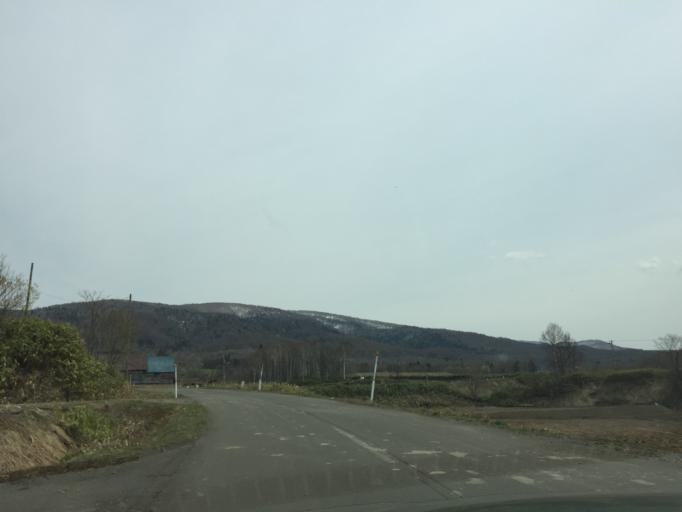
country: JP
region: Hokkaido
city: Ashibetsu
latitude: 43.6088
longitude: 142.2133
